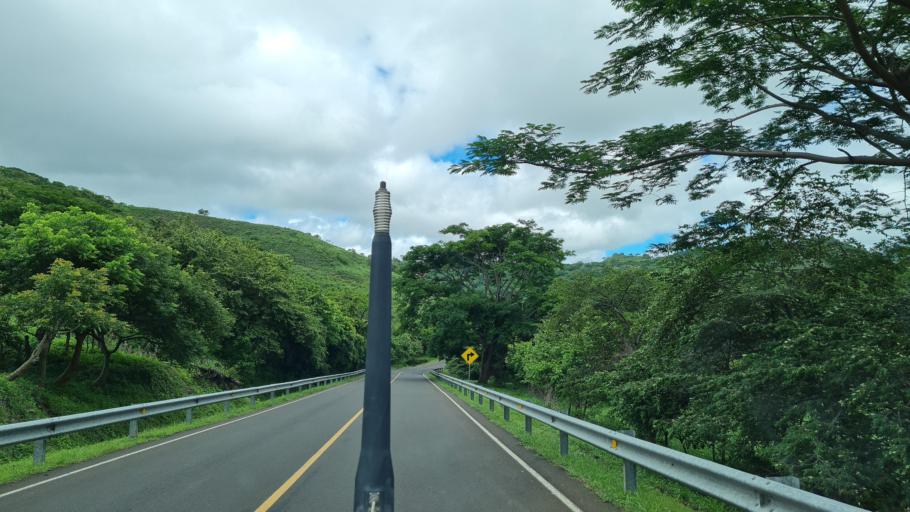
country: NI
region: Matagalpa
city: Terrabona
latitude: 12.5934
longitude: -85.9339
